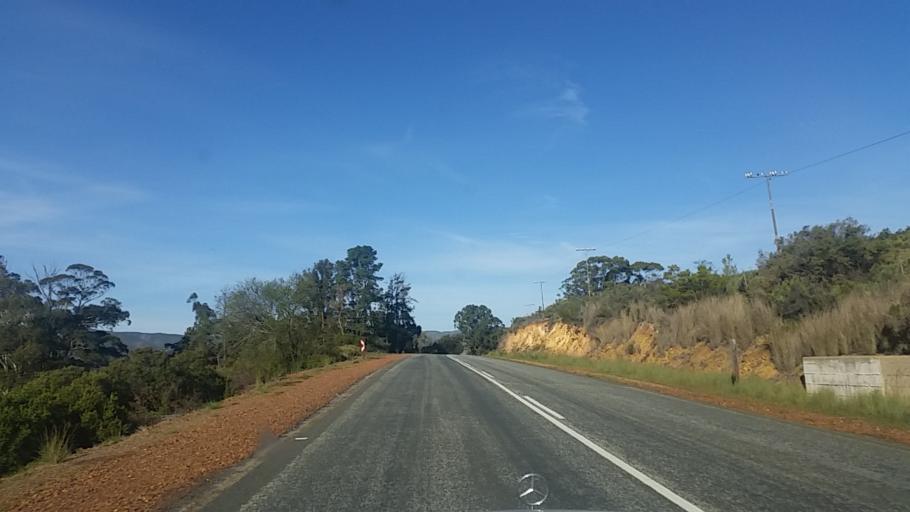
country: ZA
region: Western Cape
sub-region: Eden District Municipality
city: Knysna
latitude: -33.7732
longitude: 22.9170
